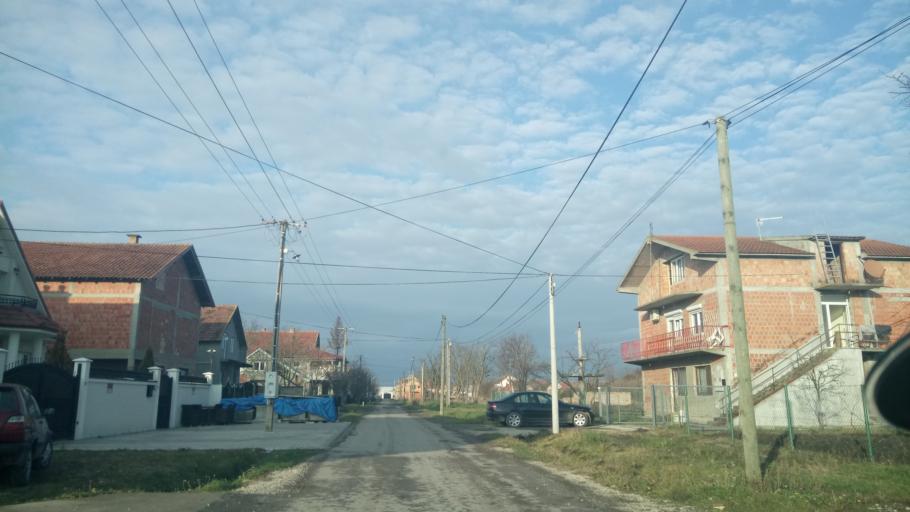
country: RS
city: Vojka
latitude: 44.9338
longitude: 20.1342
